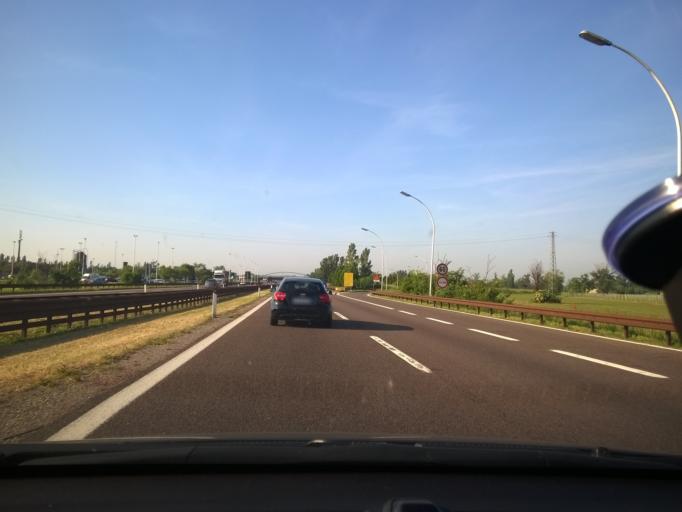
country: IT
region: Emilia-Romagna
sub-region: Provincia di Modena
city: Santa Croce Scuole
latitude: 44.7704
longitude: 10.8450
